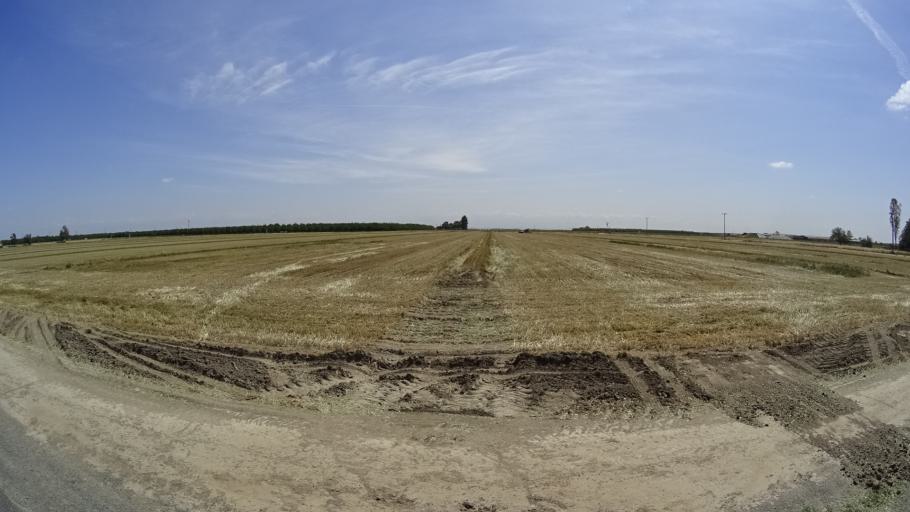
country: US
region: California
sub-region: Tulare County
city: Goshen
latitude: 36.3237
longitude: -119.4932
